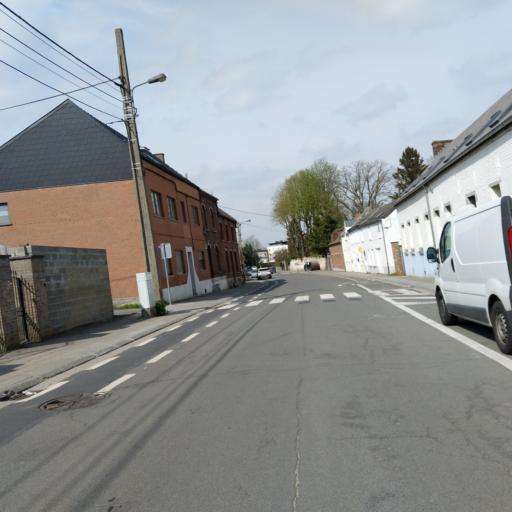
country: BE
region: Wallonia
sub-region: Province du Hainaut
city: Mons
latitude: 50.4414
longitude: 3.9625
